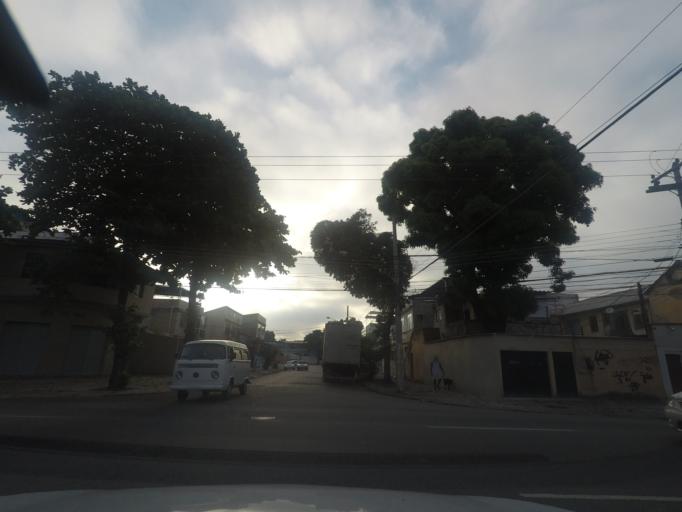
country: BR
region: Rio de Janeiro
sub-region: Duque De Caxias
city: Duque de Caxias
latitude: -22.8343
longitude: -43.2775
